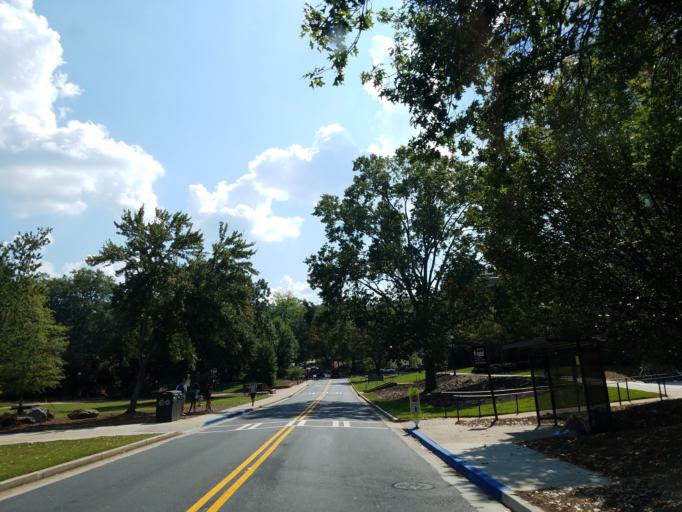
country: US
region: Georgia
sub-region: Clarke County
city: Athens
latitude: 33.9416
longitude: -83.3759
